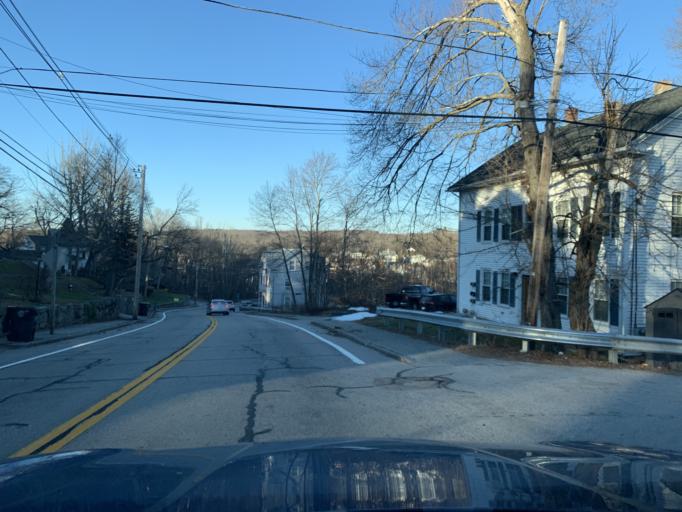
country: US
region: Rhode Island
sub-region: Kent County
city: West Warwick
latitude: 41.7191
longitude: -71.5324
